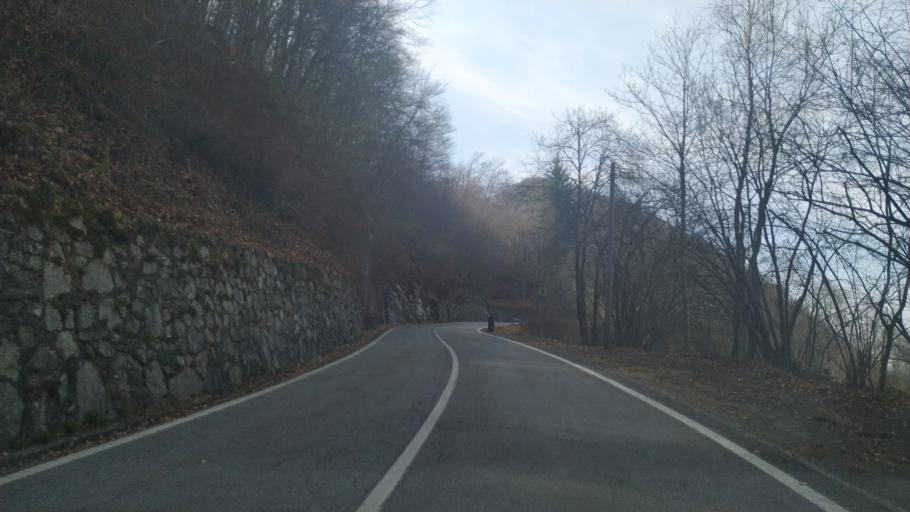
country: IT
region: Piedmont
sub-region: Provincia di Vercelli
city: Civiasco
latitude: 45.8130
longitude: 8.3091
